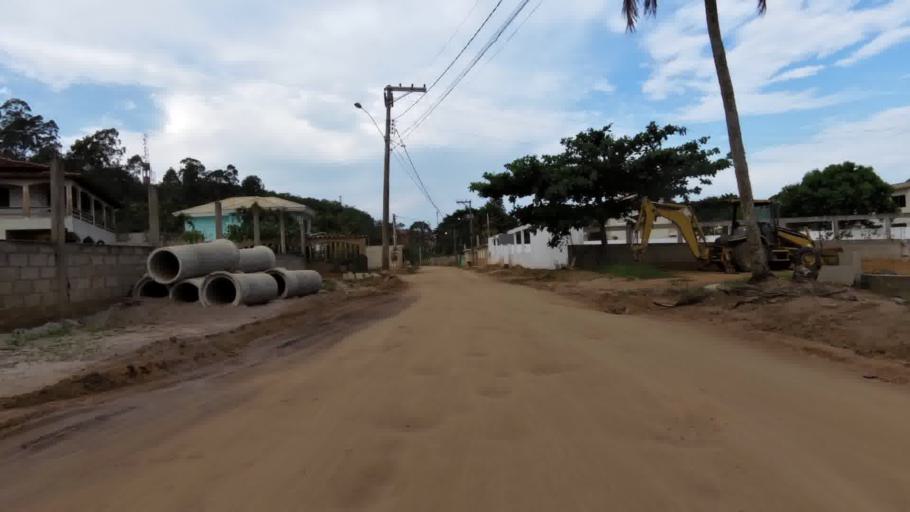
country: BR
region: Espirito Santo
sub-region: Piuma
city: Piuma
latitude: -20.8352
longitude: -40.7318
